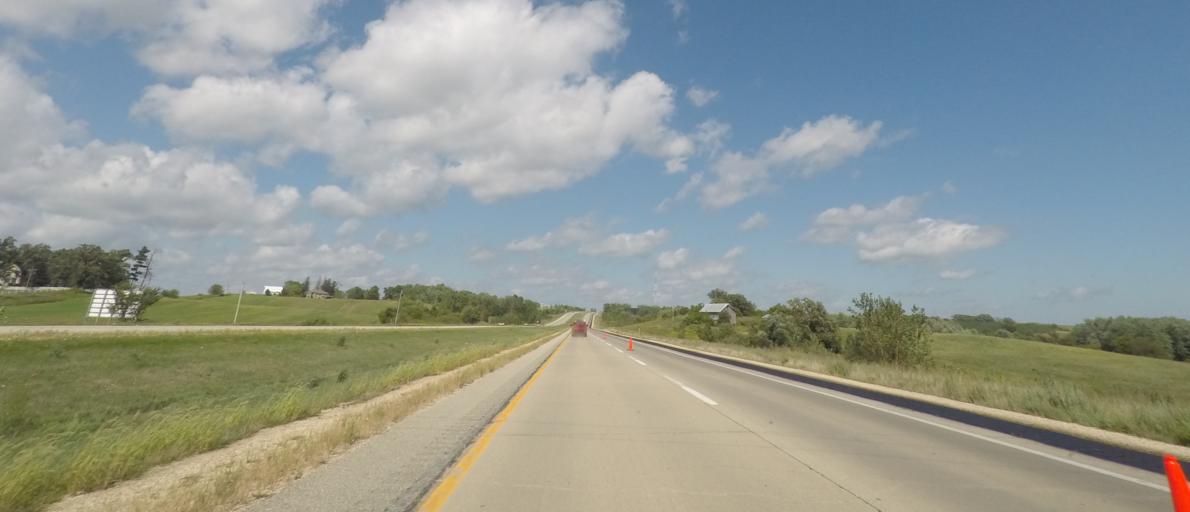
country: US
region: Iowa
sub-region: Jones County
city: Anamosa
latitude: 42.1267
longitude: -91.2600
